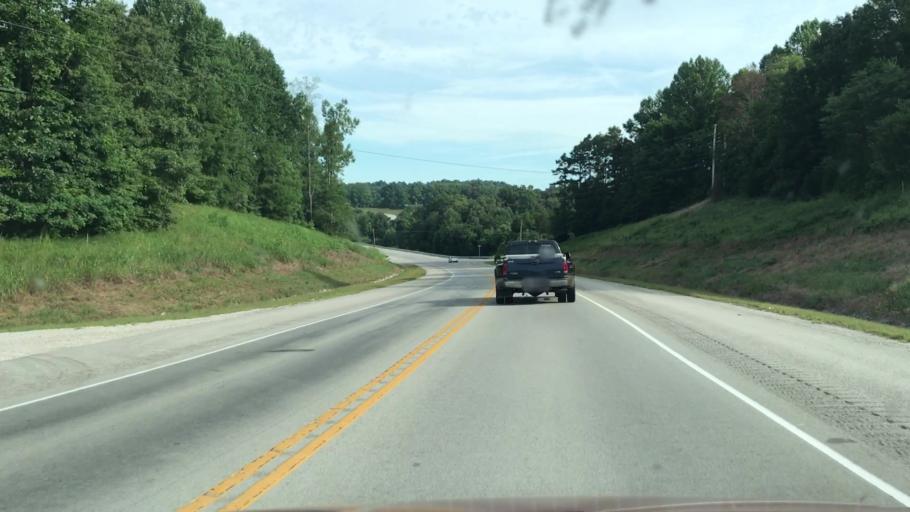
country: US
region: Kentucky
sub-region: Edmonson County
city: Brownsville
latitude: 37.1587
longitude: -86.2219
